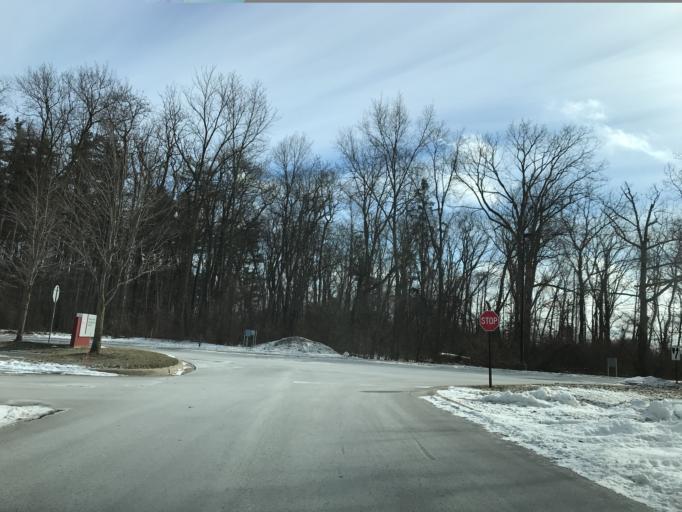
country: US
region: Michigan
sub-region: Washtenaw County
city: Ypsilanti
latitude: 42.2604
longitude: -83.6681
